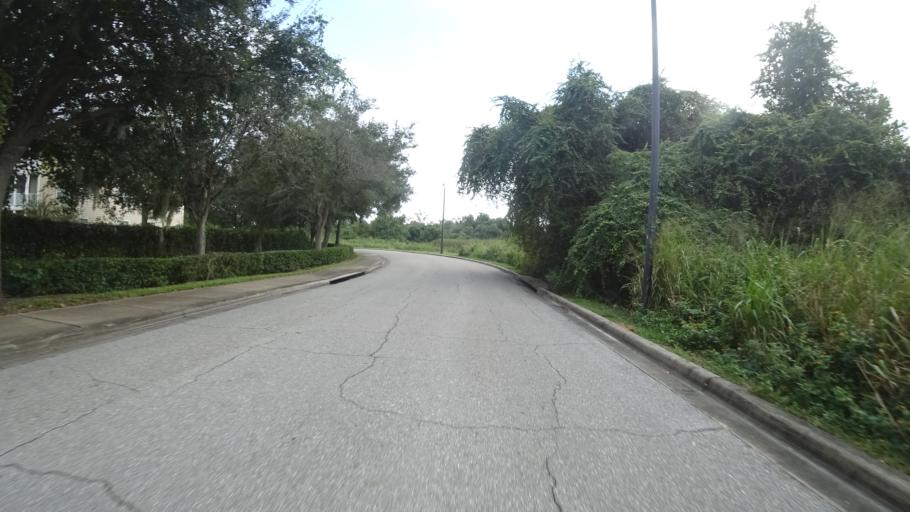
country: US
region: Florida
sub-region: Manatee County
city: South Bradenton
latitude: 27.4564
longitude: -82.6155
